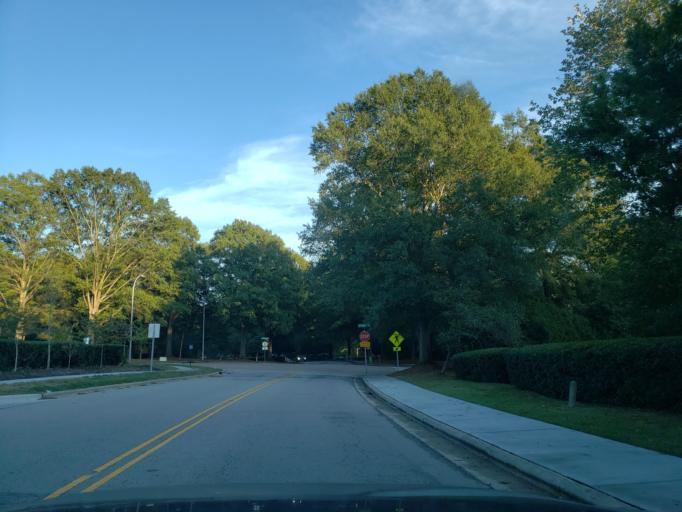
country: US
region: North Carolina
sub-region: Wake County
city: Apex
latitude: 35.7397
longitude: -78.8058
